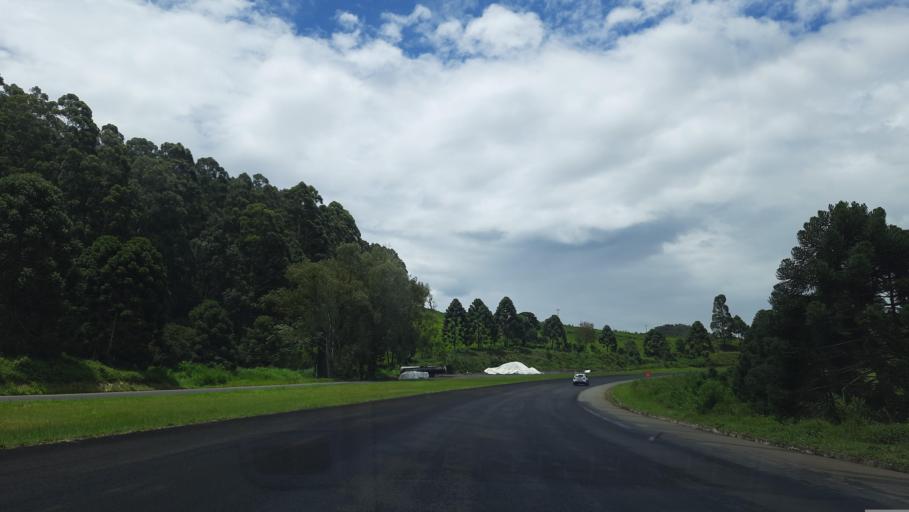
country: BR
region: Minas Gerais
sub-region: Pocos De Caldas
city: Pocos de Caldas
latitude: -21.8271
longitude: -46.6717
